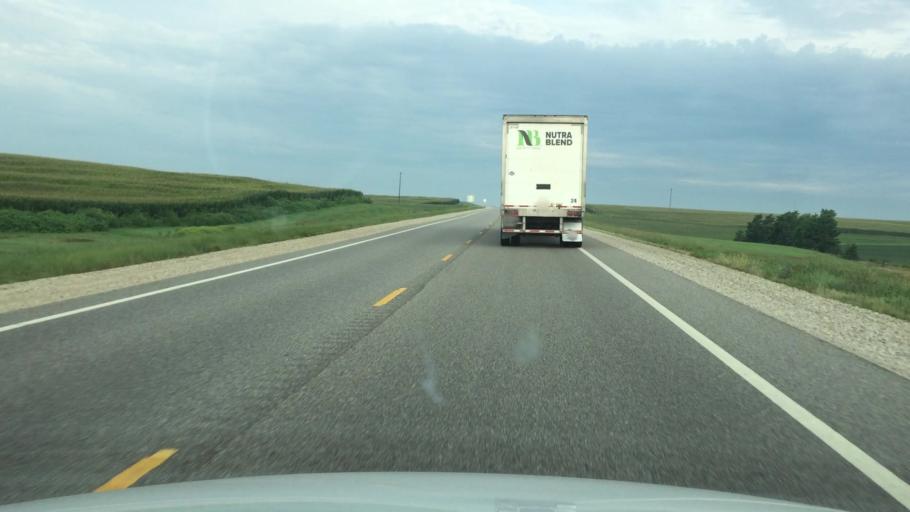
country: US
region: Kansas
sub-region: Doniphan County
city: Highland
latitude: 39.8421
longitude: -95.2795
